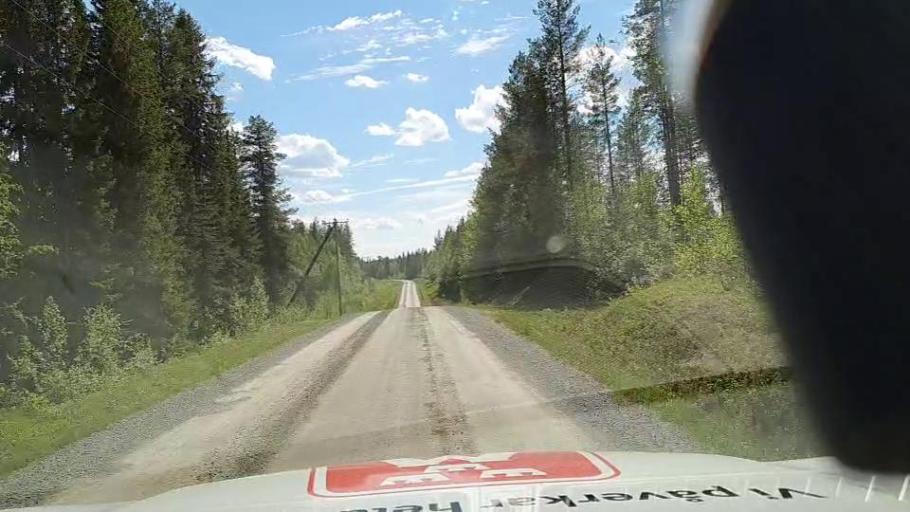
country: SE
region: Jaemtland
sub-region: Stroemsunds Kommun
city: Stroemsund
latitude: 64.4642
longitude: 15.5939
